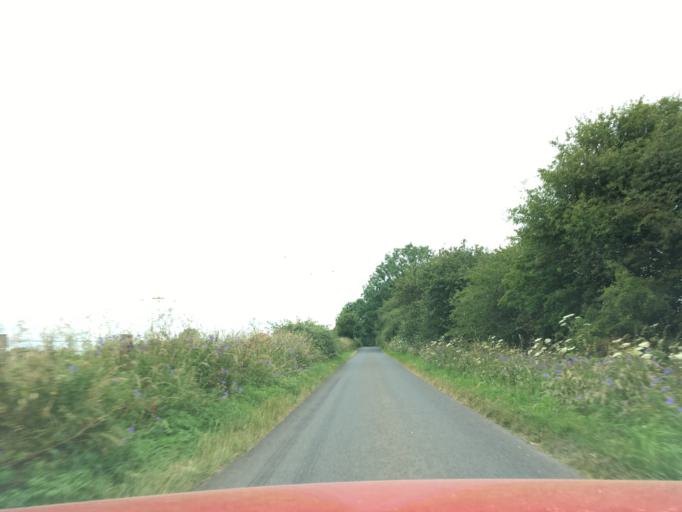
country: GB
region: England
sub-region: Gloucestershire
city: Shipton Village
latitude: 51.8940
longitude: -1.9145
